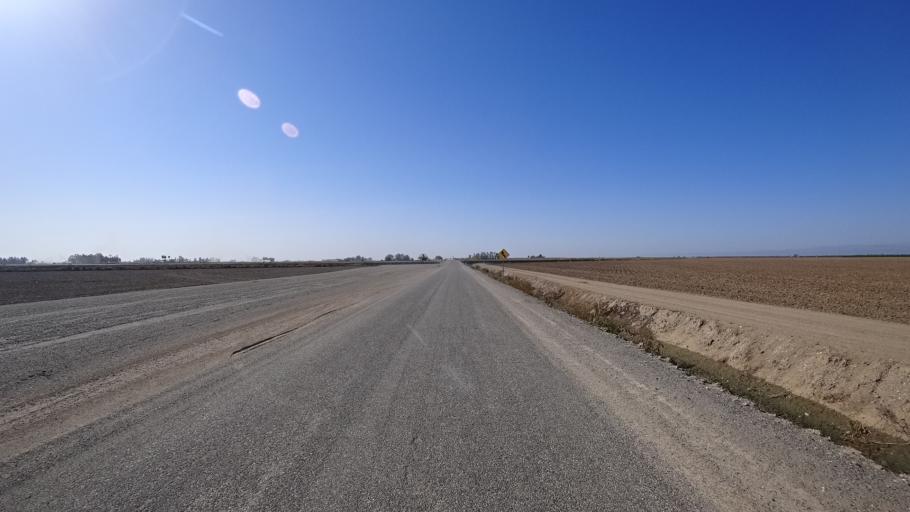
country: US
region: California
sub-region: Glenn County
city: Willows
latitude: 39.5889
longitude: -122.1170
